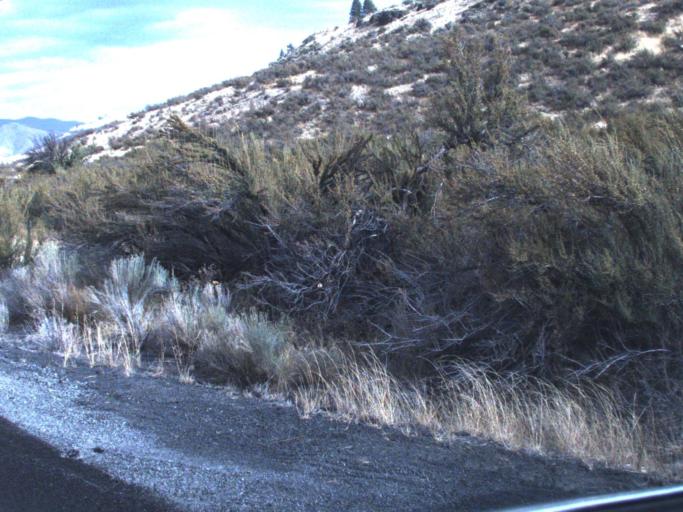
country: US
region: Washington
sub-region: Okanogan County
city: Coulee Dam
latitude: 47.8946
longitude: -118.7142
